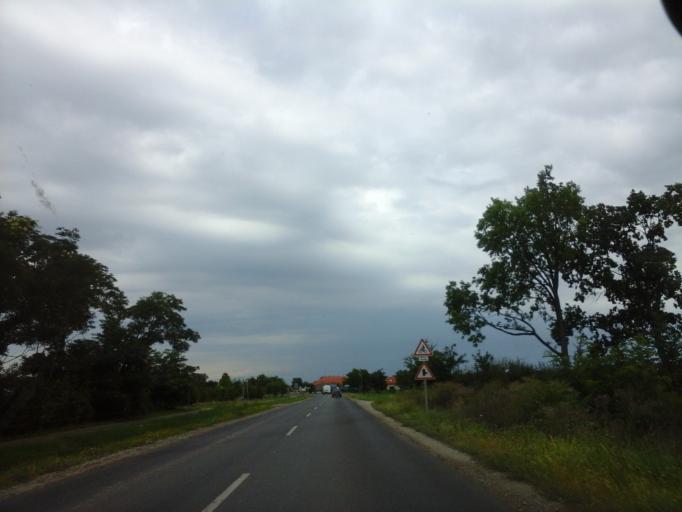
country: HU
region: Hajdu-Bihar
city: Balmazujvaros
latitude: 47.5976
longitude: 21.3386
